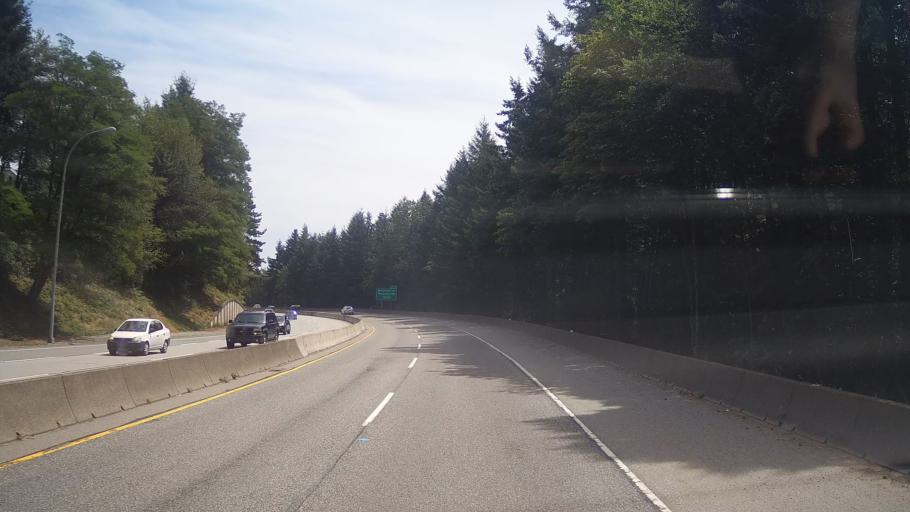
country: CA
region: British Columbia
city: West Vancouver
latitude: 49.3497
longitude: -123.2432
